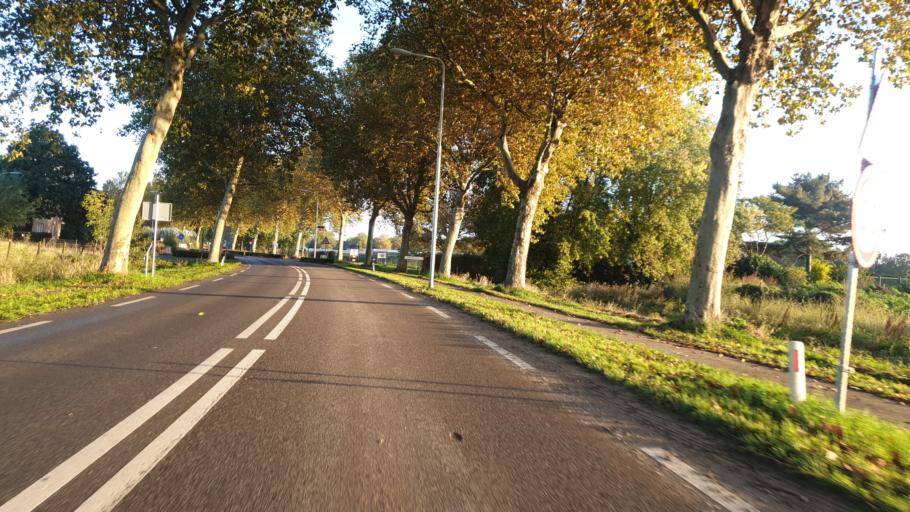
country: NL
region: Gelderland
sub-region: Gemeente Druten
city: Druten
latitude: 51.8788
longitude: 5.6107
